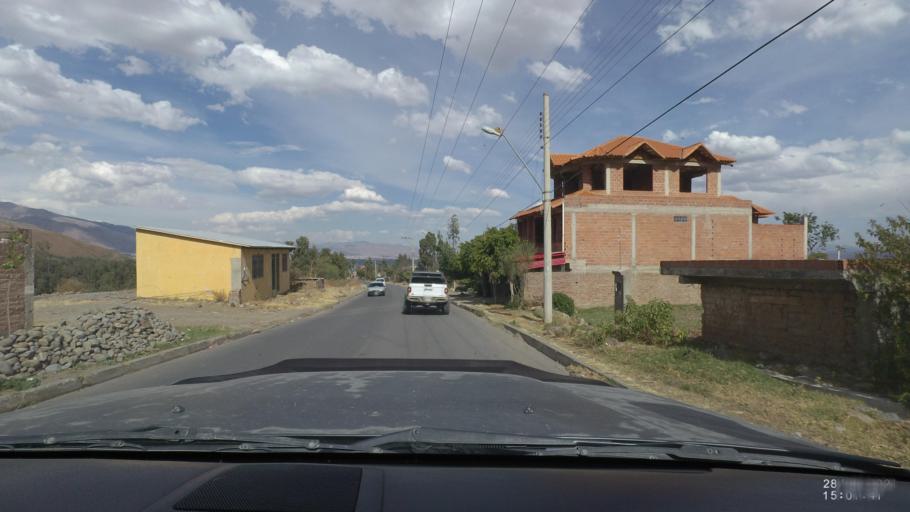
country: BO
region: Cochabamba
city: Cochabamba
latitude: -17.3114
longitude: -66.2906
